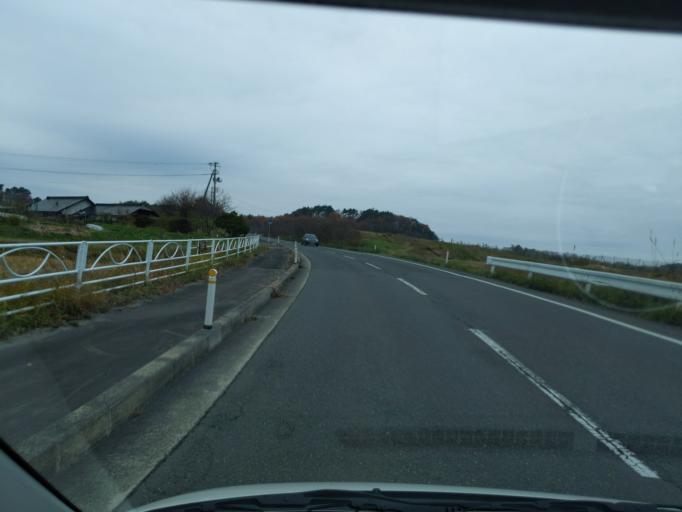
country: JP
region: Iwate
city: Mizusawa
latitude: 39.1996
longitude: 141.2218
